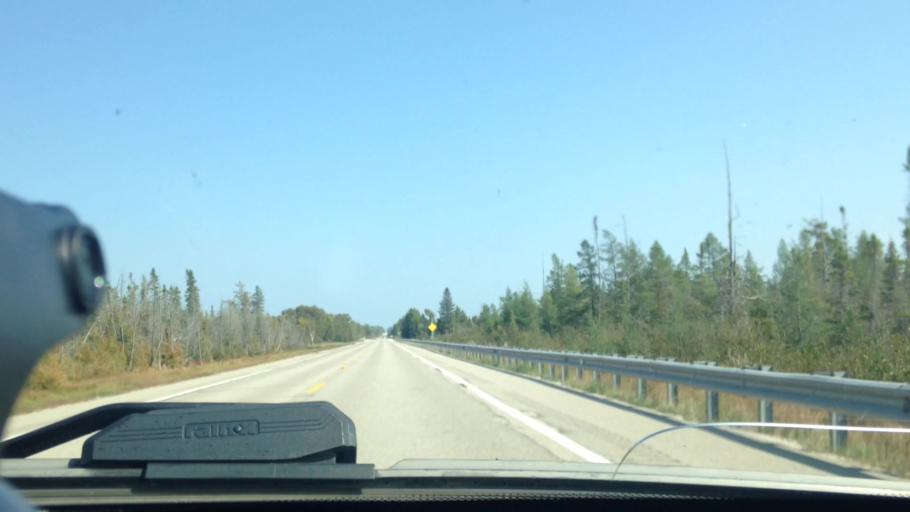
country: US
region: Michigan
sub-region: Luce County
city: Newberry
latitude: 46.3035
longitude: -85.3274
